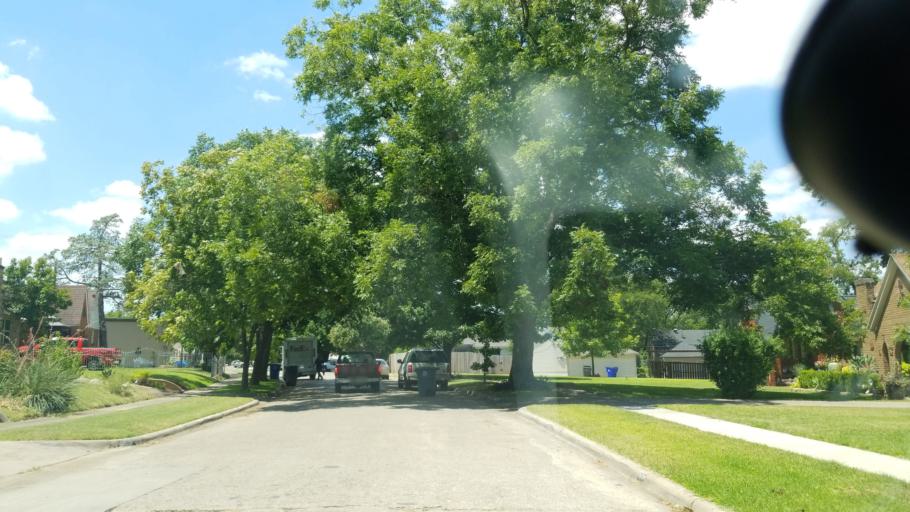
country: US
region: Texas
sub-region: Dallas County
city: Cockrell Hill
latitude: 32.7281
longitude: -96.8432
